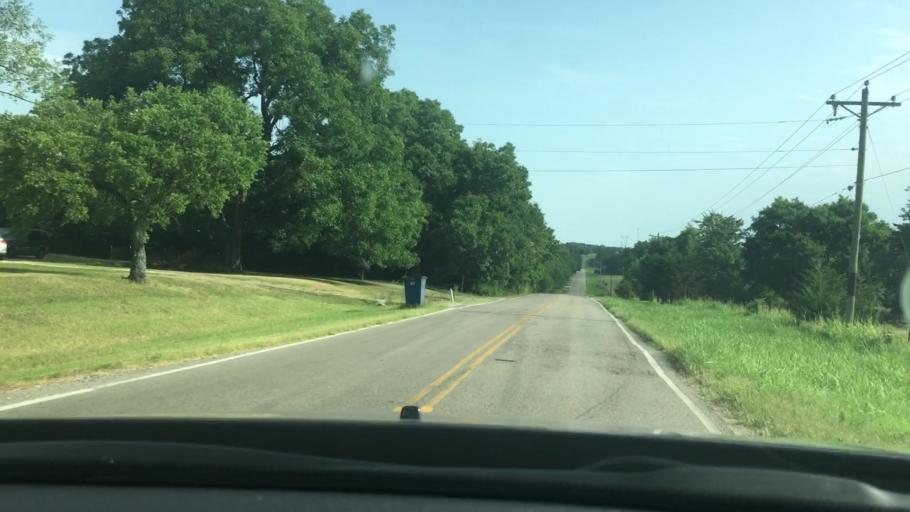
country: US
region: Oklahoma
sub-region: Pontotoc County
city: Byng
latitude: 34.8555
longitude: -96.6135
